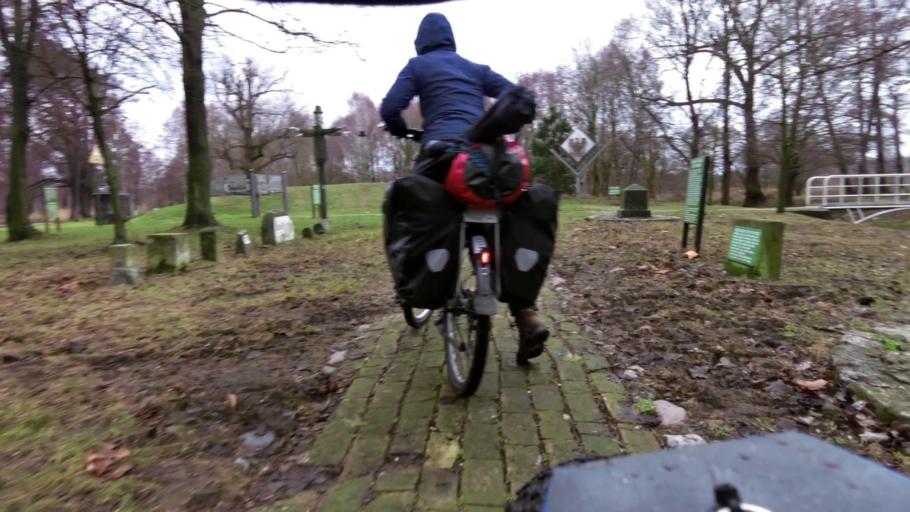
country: PL
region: Lubusz
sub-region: Powiat gorzowski
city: Witnica
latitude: 52.6754
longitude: 14.8970
